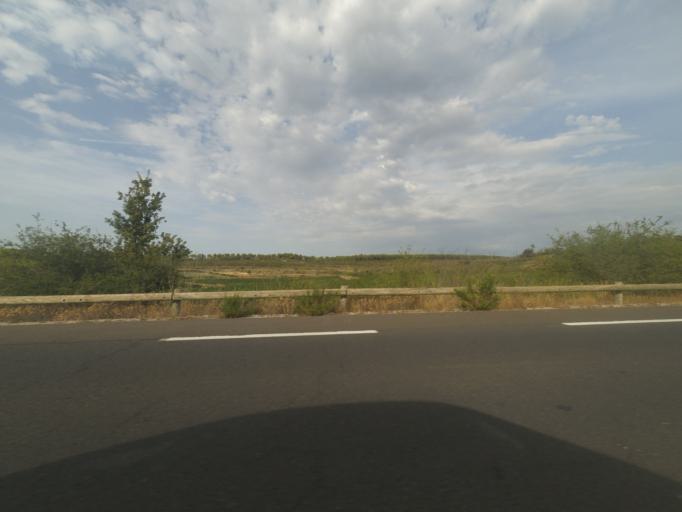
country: FR
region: Languedoc-Roussillon
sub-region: Departement de l'Herault
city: Assas
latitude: 43.7142
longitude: 3.9170
